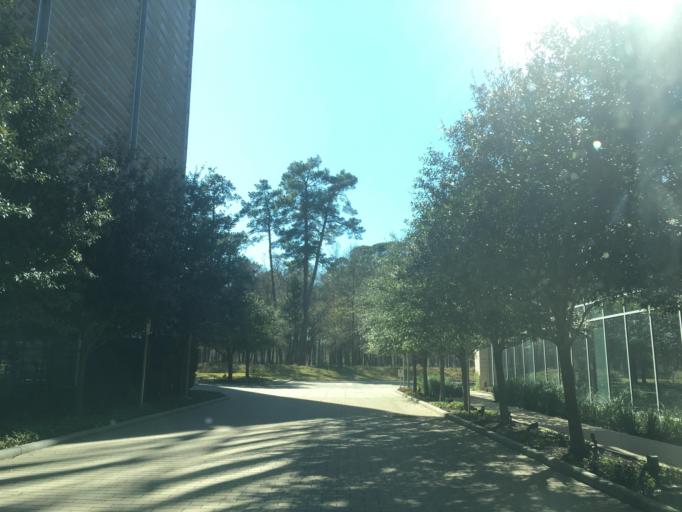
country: US
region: Texas
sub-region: Harris County
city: Spring
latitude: 30.0977
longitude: -95.4419
